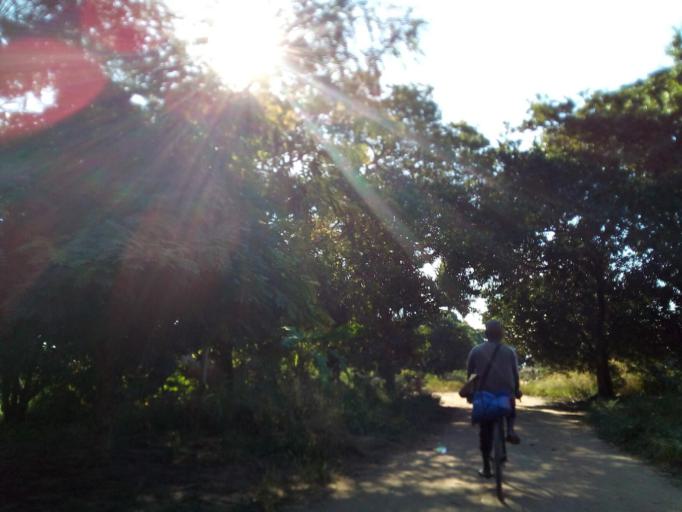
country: MZ
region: Zambezia
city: Quelimane
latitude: -17.5337
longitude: 36.6860
